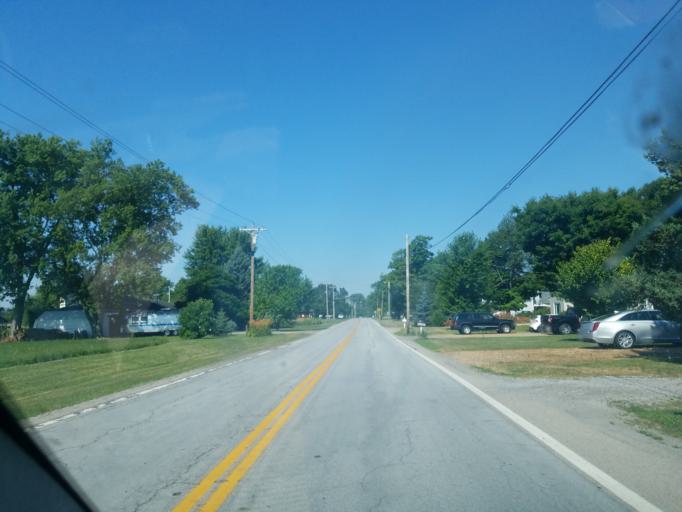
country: US
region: Ohio
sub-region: Logan County
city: Northwood
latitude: 40.4375
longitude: -83.8008
